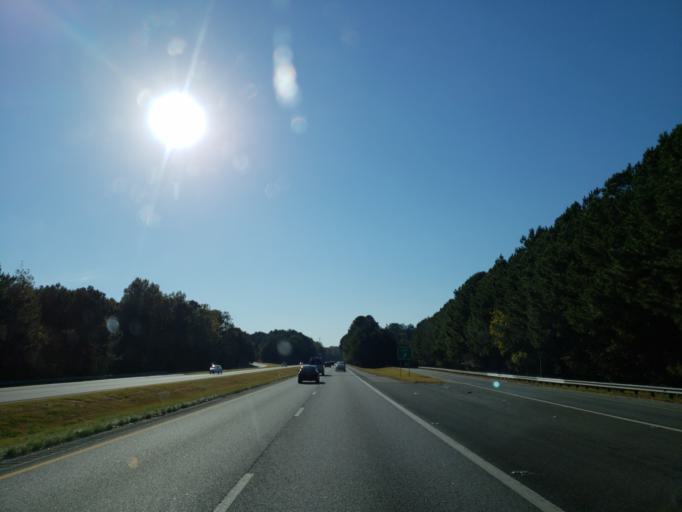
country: US
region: Georgia
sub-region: Gwinnett County
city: Lawrenceville
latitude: 33.9616
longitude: -84.0290
